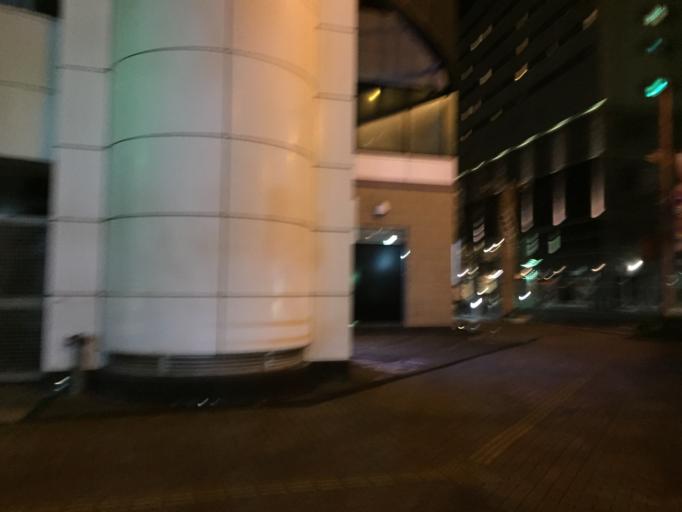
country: JP
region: Shizuoka
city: Numazu
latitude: 35.0964
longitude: 138.8576
